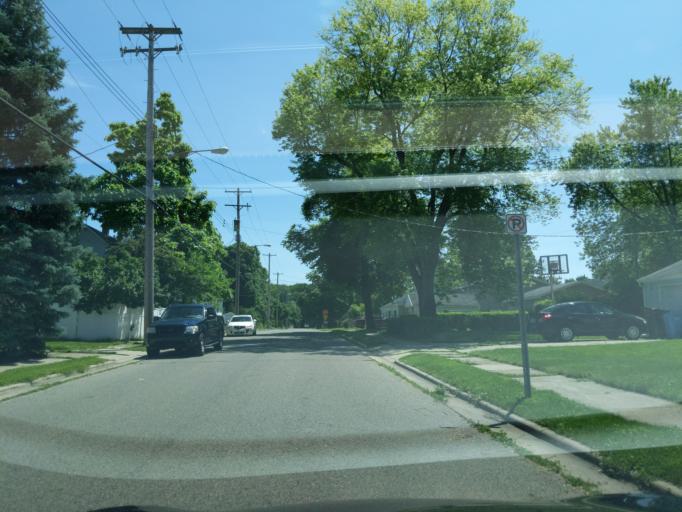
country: US
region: Michigan
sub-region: Ingham County
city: Lansing
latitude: 42.7517
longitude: -84.5345
